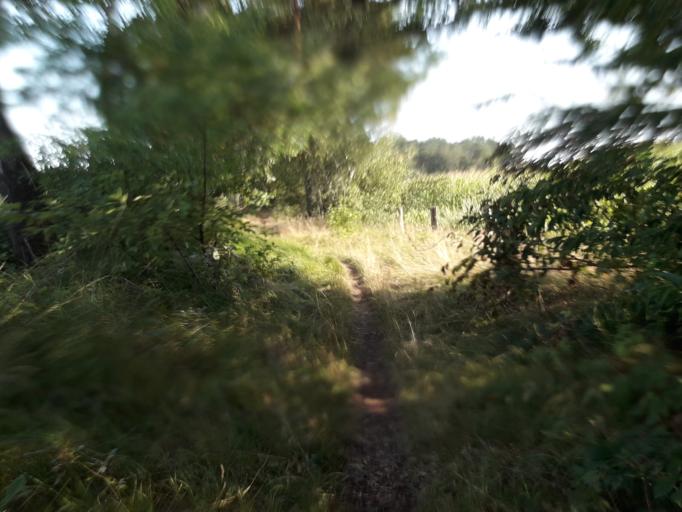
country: DE
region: North Rhine-Westphalia
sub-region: Regierungsbezirk Detmold
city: Hovelhof
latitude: 51.7917
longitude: 8.6735
